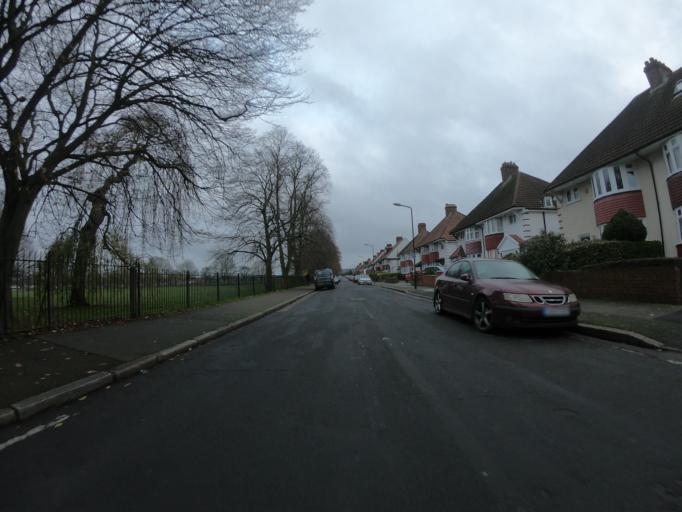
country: GB
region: England
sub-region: Greater London
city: Woolwich
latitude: 51.4794
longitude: 0.0389
